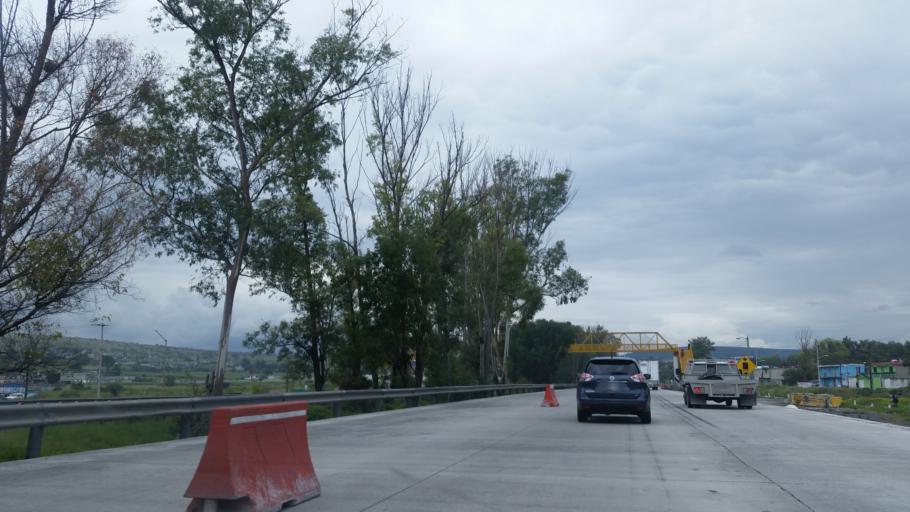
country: MX
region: Mexico
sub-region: Huehuetoca
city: Villa URBI del Rey
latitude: 19.8381
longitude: -99.2745
